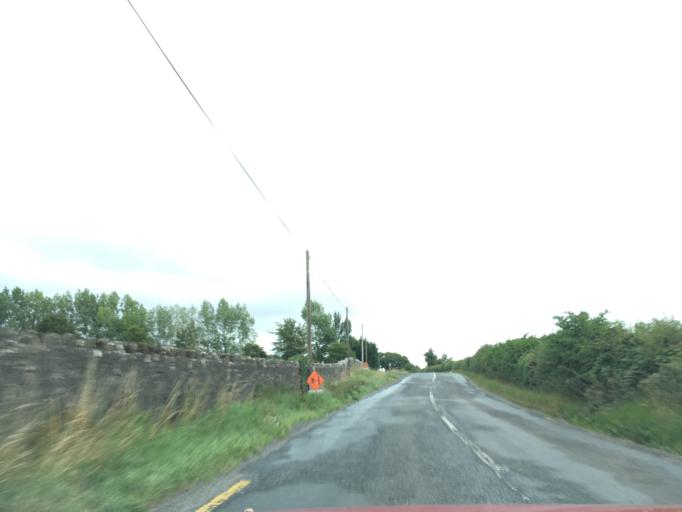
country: IE
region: Munster
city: Cashel
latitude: 52.4458
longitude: -7.8051
